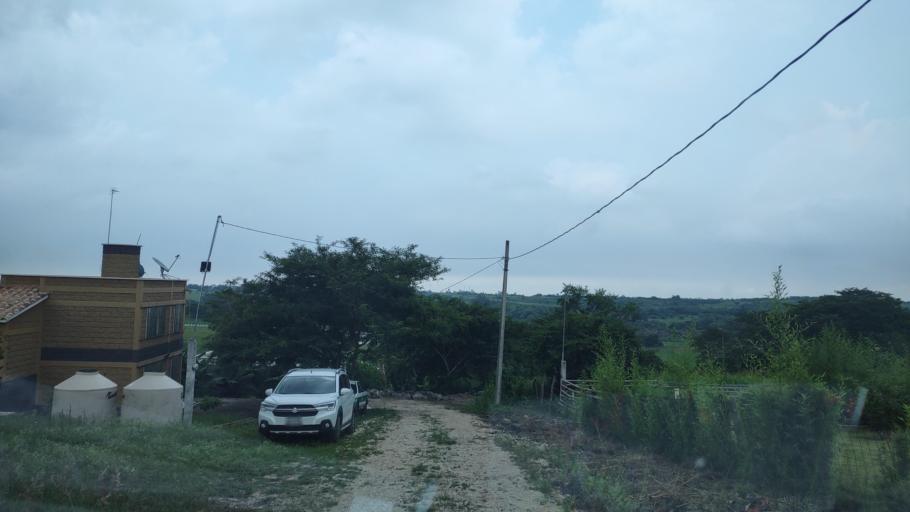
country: MX
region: Veracruz
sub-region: Emiliano Zapata
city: Dos Rios
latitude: 19.4771
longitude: -96.8137
